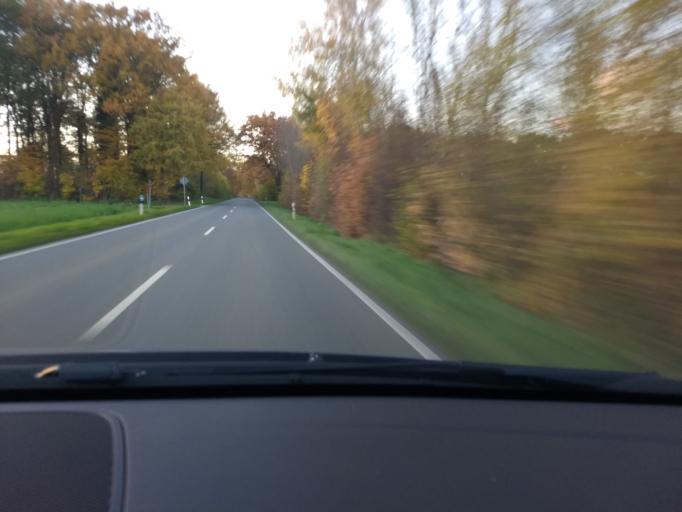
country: DE
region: North Rhine-Westphalia
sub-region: Regierungsbezirk Munster
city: Heiden
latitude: 51.8375
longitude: 6.9141
